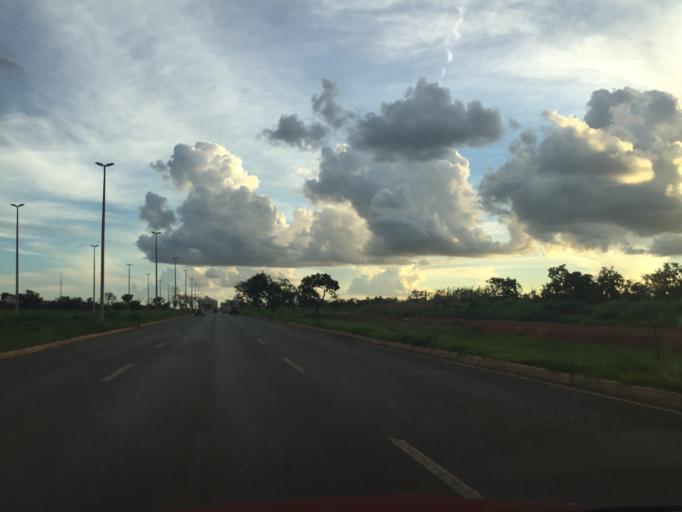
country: BR
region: Federal District
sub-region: Brasilia
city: Brasilia
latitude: -15.8040
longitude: -47.9919
